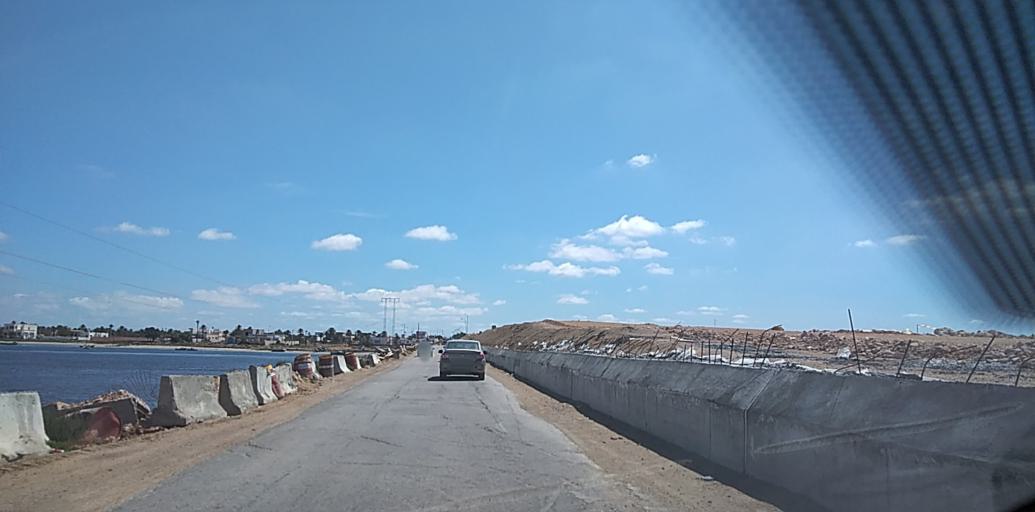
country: TN
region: Safaqis
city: Al Qarmadah
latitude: 34.6621
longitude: 11.1229
